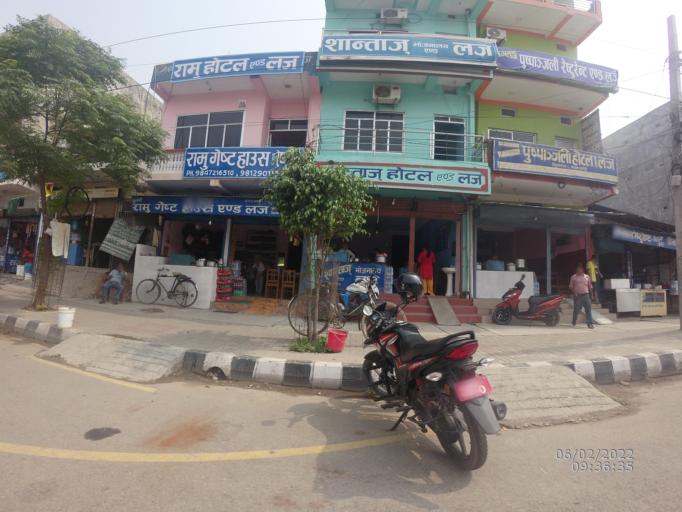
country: NP
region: Western Region
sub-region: Lumbini Zone
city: Bhairahawa
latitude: 27.4974
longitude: 83.4578
